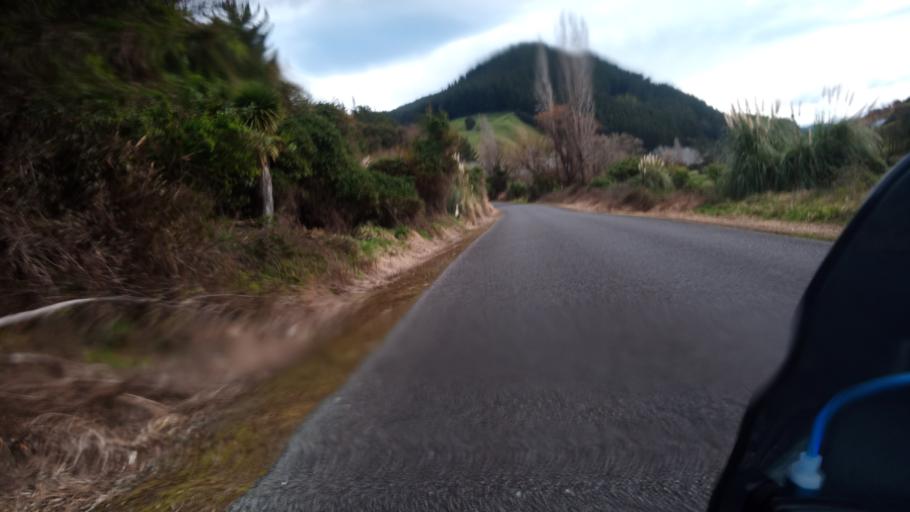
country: NZ
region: Hawke's Bay
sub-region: Wairoa District
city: Wairoa
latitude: -38.8249
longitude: 177.5077
